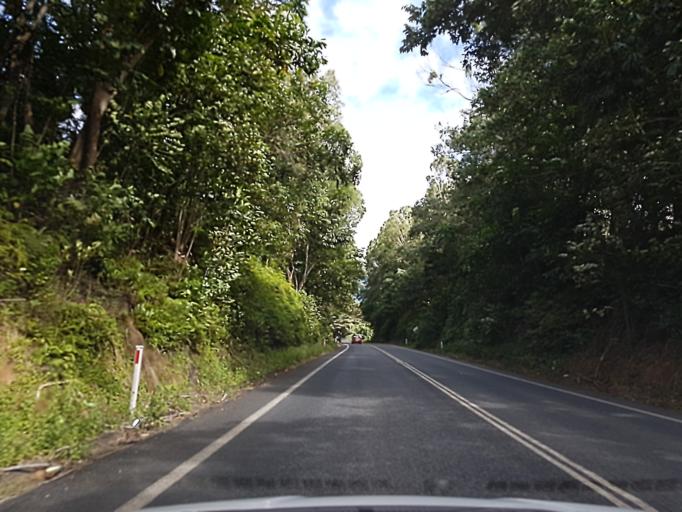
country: AU
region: Queensland
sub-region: Cairns
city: Port Douglas
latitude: -16.4783
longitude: 145.3964
